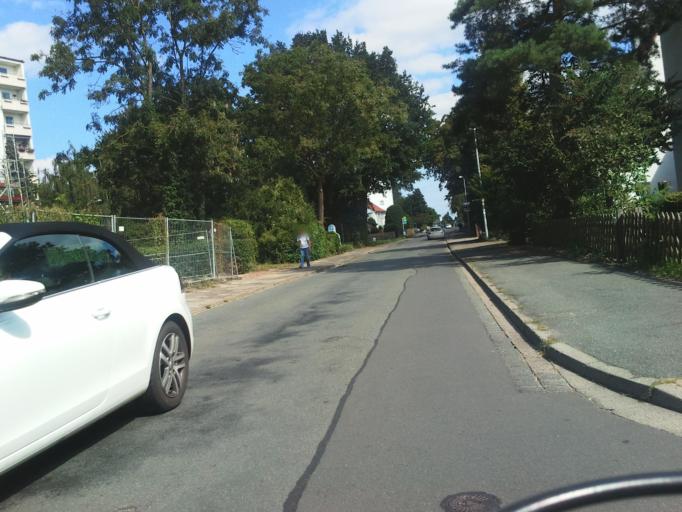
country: DE
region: Lower Saxony
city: Nienburg
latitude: 52.6347
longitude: 9.2163
